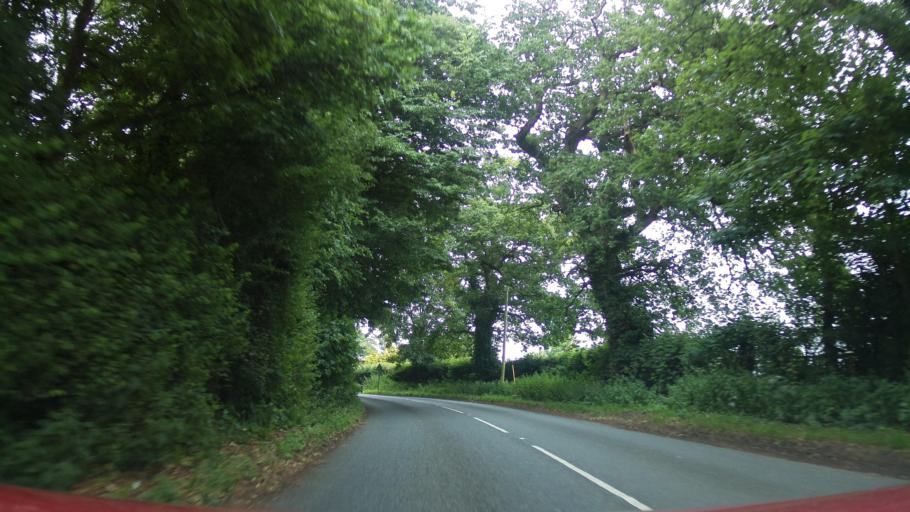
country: GB
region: England
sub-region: Somerset
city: Crewkerne
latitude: 50.8802
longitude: -2.7503
